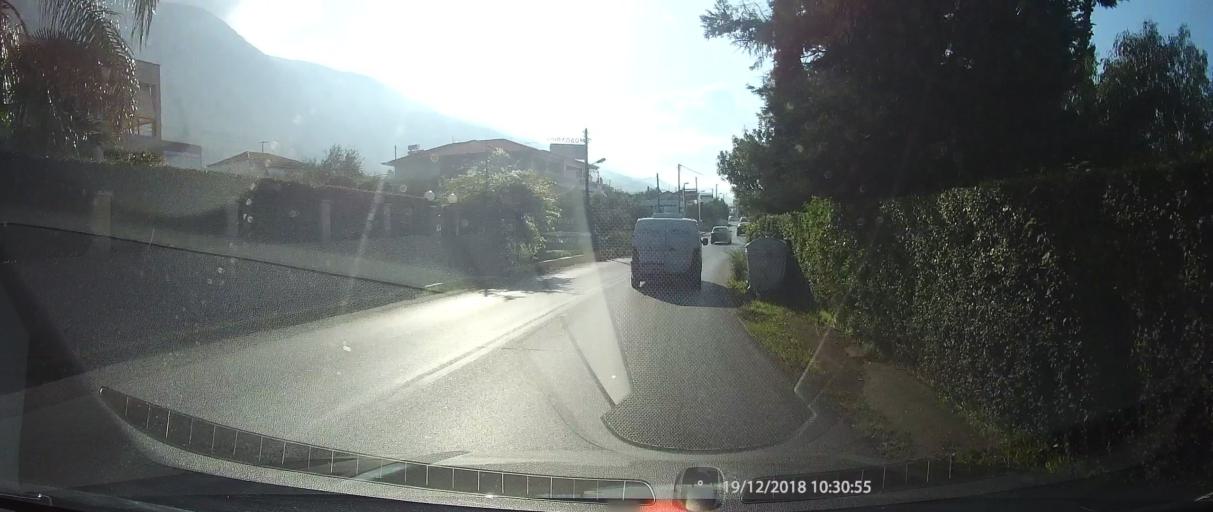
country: GR
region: Peloponnese
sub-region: Nomos Messinias
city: Paralia Vergas
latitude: 37.0126
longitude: 22.1544
